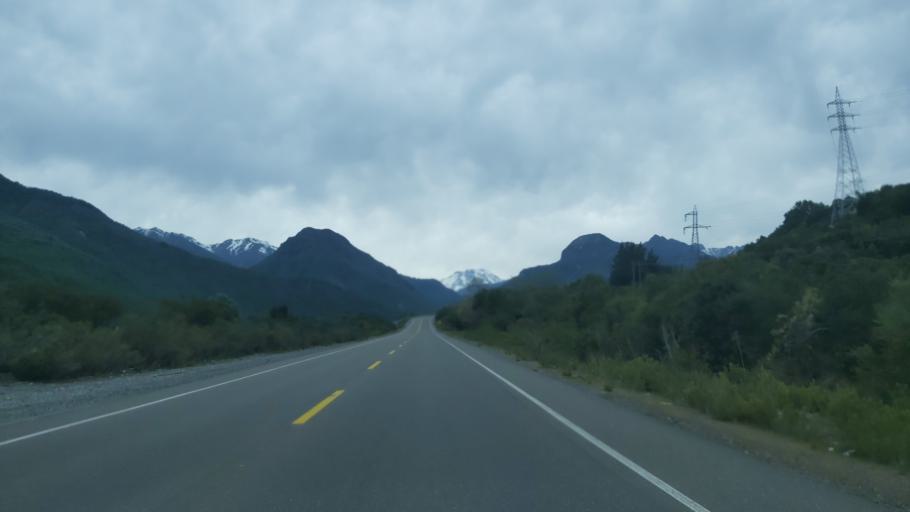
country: CL
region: Maule
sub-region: Provincia de Linares
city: Colbun
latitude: -35.7092
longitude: -71.1059
